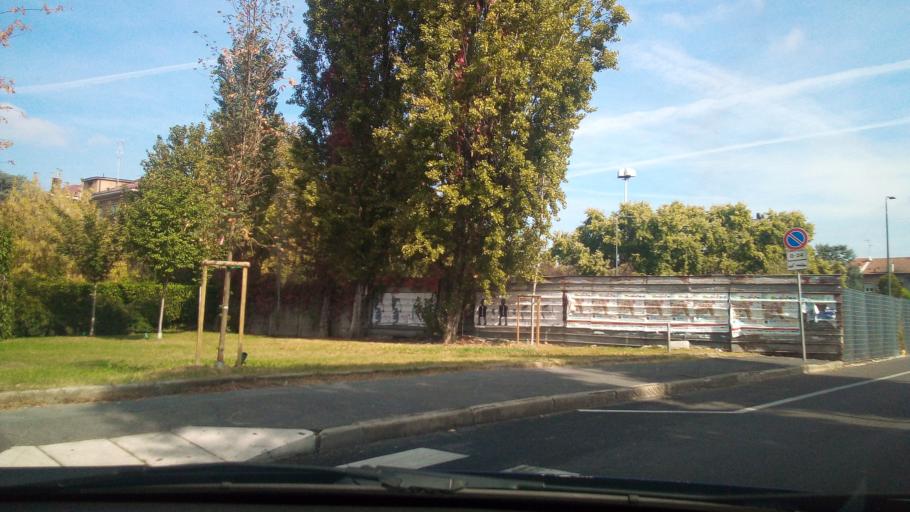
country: IT
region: Lombardy
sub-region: Citta metropolitana di Milano
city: Sesto San Giovanni
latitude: 45.5107
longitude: 9.2297
